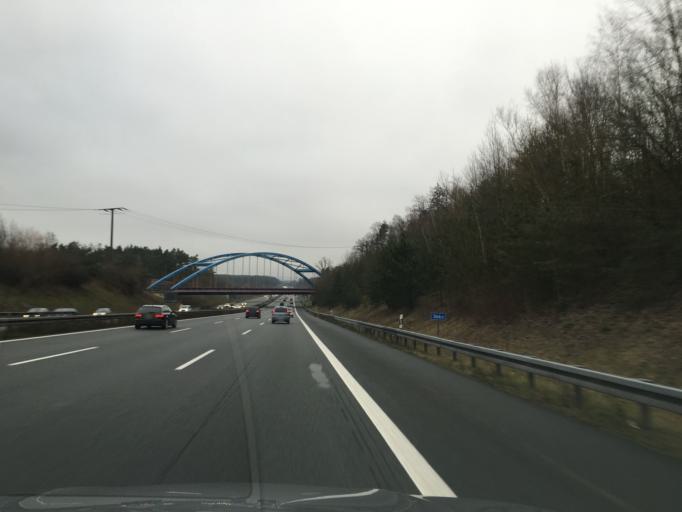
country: DE
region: Bavaria
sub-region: Regierungsbezirk Mittelfranken
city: Lauf an der Pegnitz
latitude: 49.5090
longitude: 11.2972
